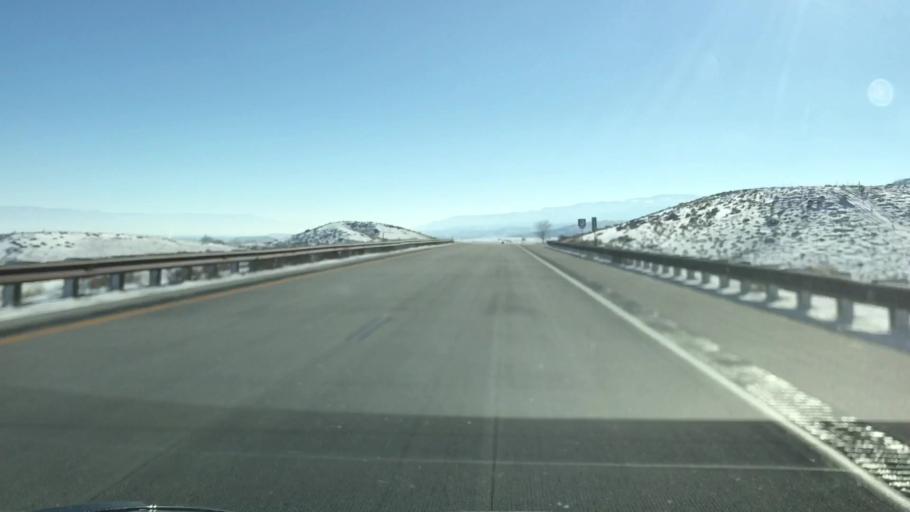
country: US
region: Colorado
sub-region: Mesa County
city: Loma
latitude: 39.1933
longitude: -108.8437
